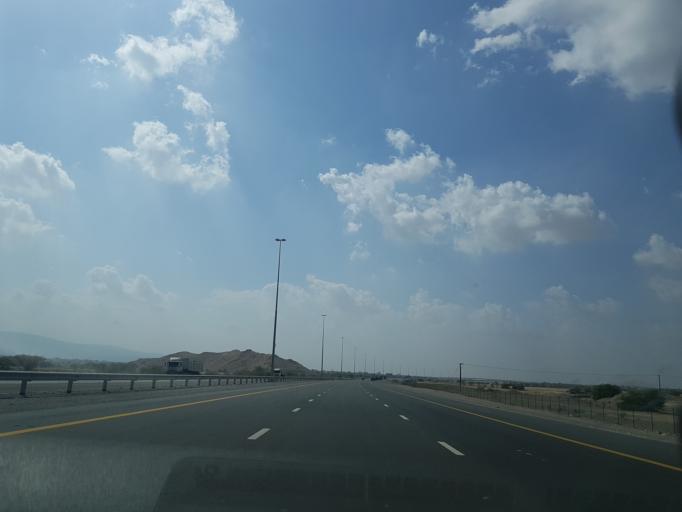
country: AE
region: Ra's al Khaymah
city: Ras al-Khaimah
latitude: 25.7353
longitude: 56.0150
